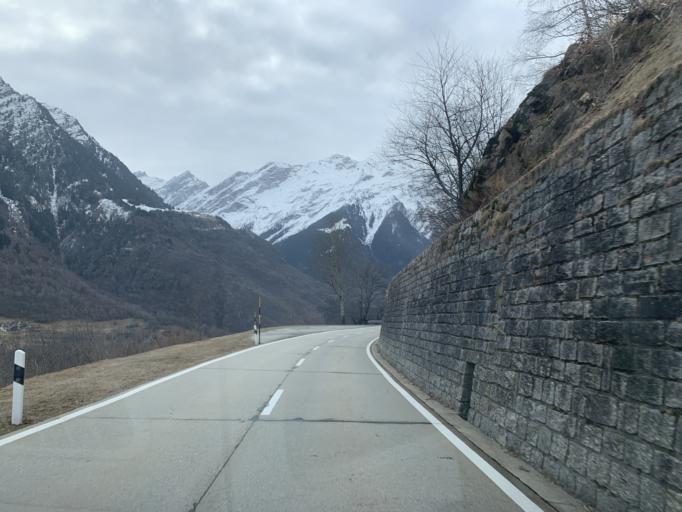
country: CH
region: Ticino
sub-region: Blenio District
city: Acquarossa
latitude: 46.5185
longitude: 8.9331
